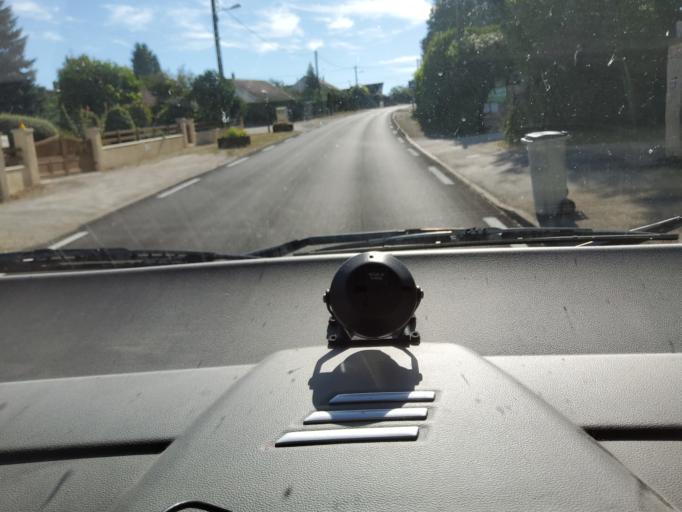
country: FR
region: Franche-Comte
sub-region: Departement du Jura
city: Champvans
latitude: 47.1054
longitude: 5.4482
